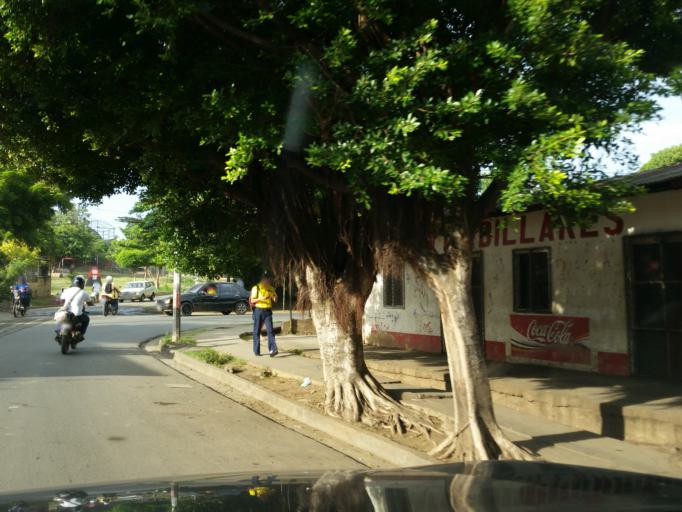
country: NI
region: Managua
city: Managua
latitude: 12.1050
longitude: -86.2236
